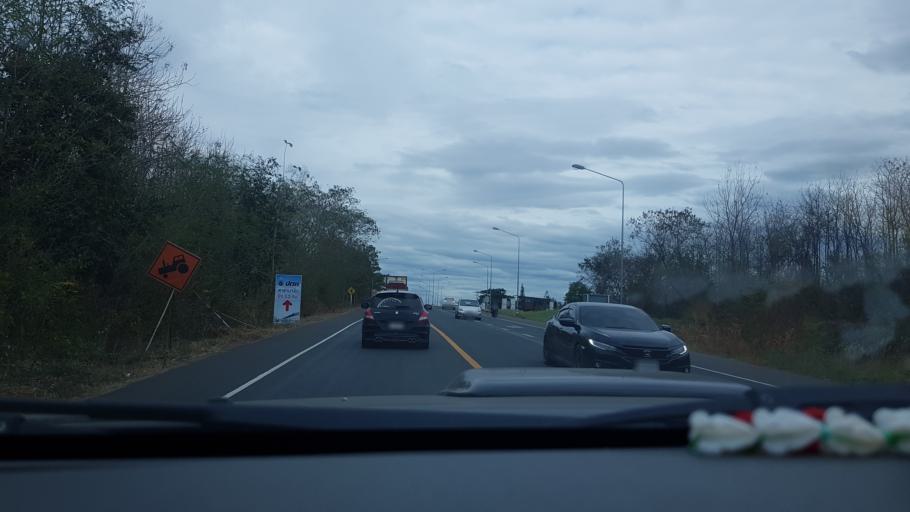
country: TH
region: Phetchabun
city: Phetchabun
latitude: 16.4850
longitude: 101.1377
